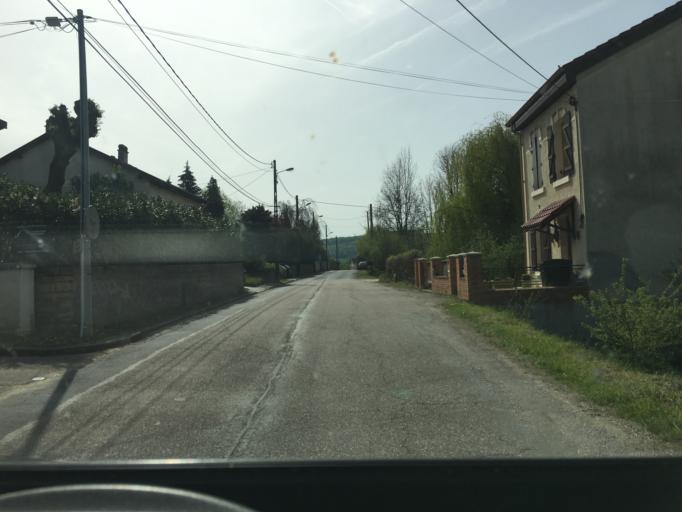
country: FR
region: Lorraine
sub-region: Departement de Meurthe-et-Moselle
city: Chaligny
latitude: 48.6329
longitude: 6.0479
